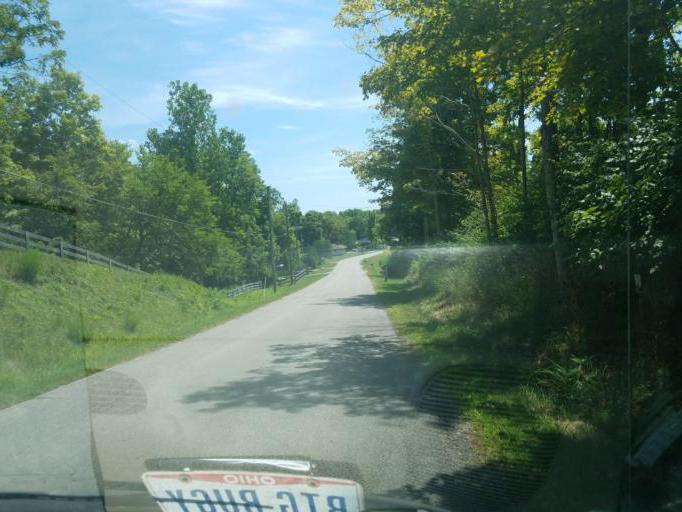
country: US
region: Ohio
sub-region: Franklin County
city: Grove City
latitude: 39.8524
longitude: -83.1931
